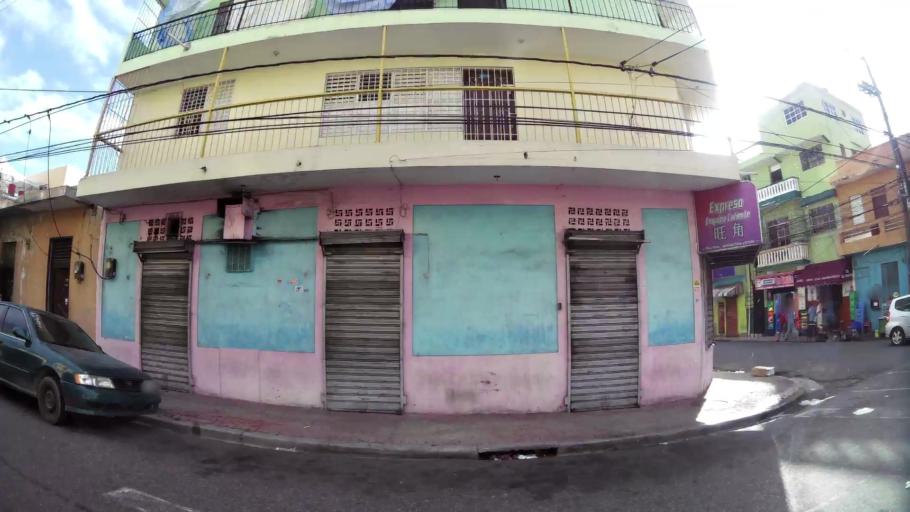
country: DO
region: Nacional
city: San Carlos
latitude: 18.4777
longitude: -69.8894
